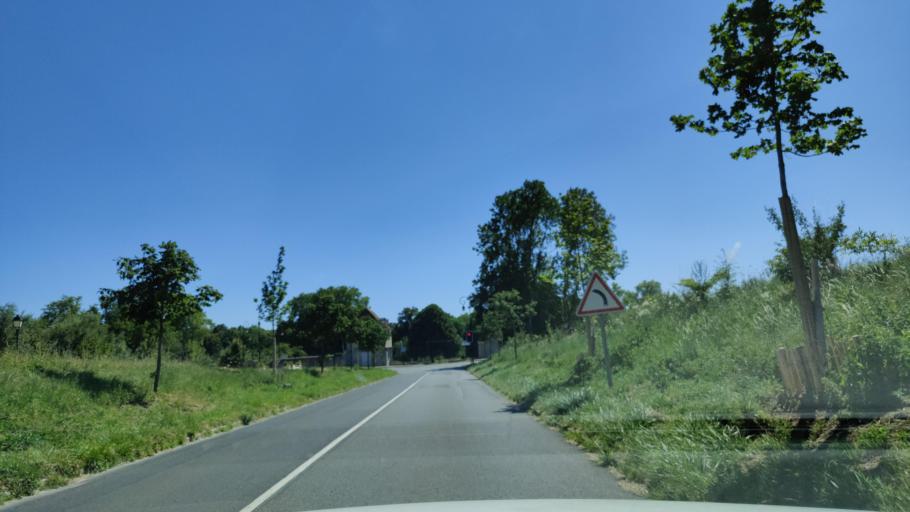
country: FR
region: Ile-de-France
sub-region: Departement de l'Essonne
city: Fontenay-les-Briis
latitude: 48.6097
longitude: 2.1659
